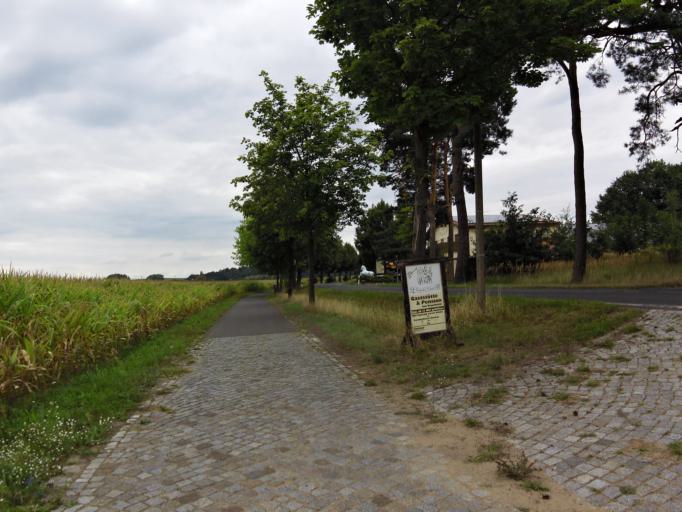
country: DE
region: Saxony
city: Meissen
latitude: 51.2144
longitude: 13.4090
